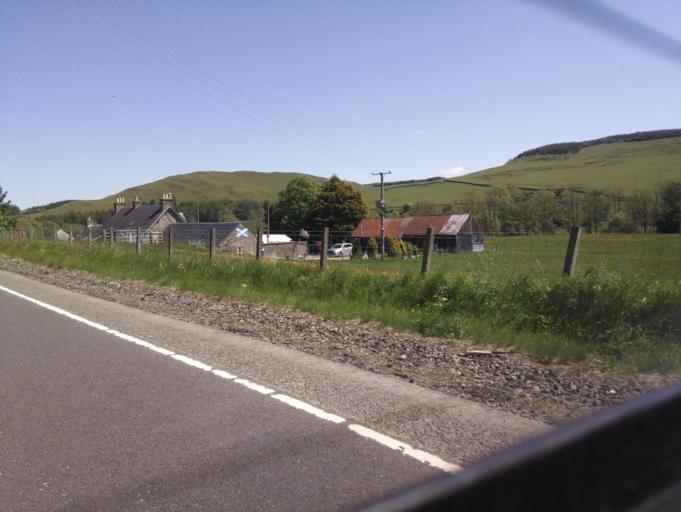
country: GB
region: Scotland
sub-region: The Scottish Borders
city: Hawick
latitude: 55.3868
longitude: -2.8624
